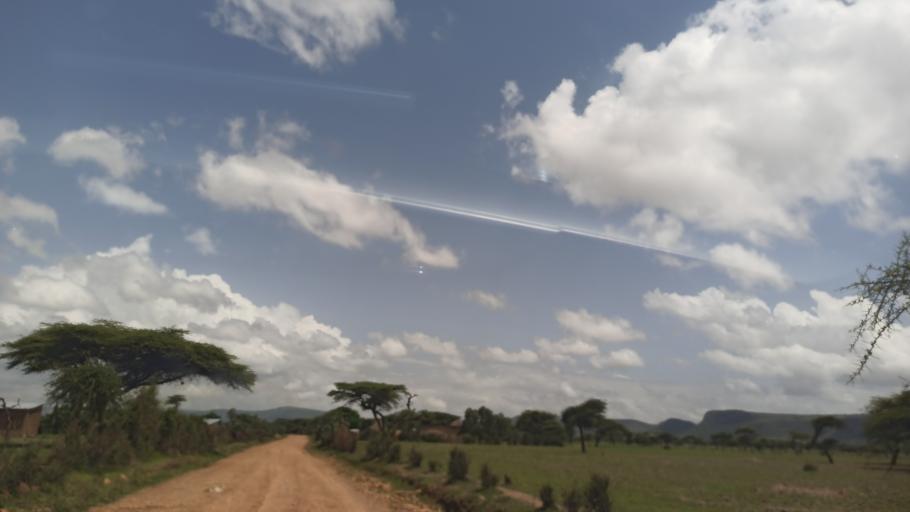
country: ET
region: Oromiya
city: Ziway
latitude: 7.9147
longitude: 38.6638
